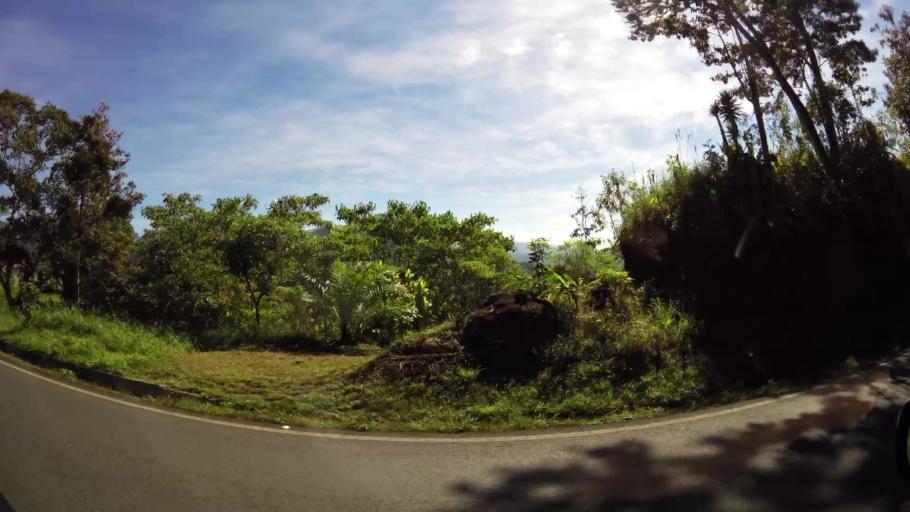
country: CR
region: San Jose
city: San Isidro
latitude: 9.4328
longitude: -83.7102
